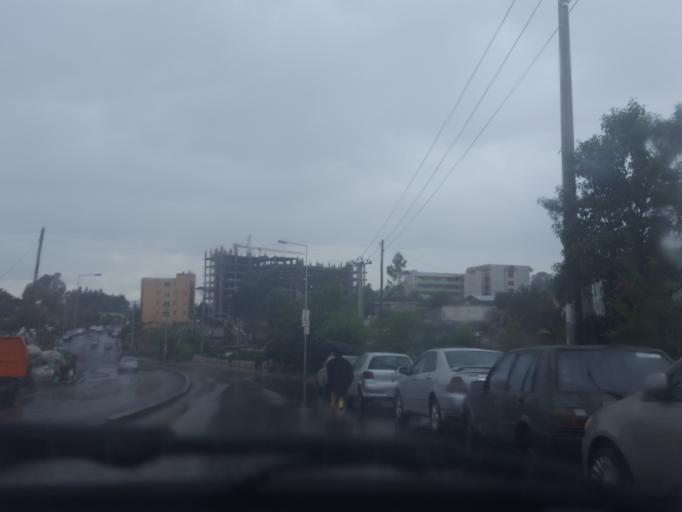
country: ET
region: Adis Abeba
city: Addis Ababa
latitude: 9.0285
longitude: 38.7814
